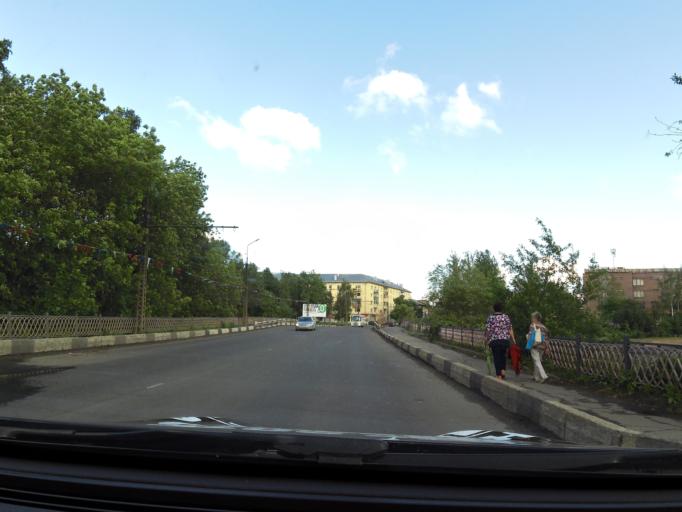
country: RU
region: Republic of Karelia
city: Petrozavodsk
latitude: 61.7862
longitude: 34.3879
